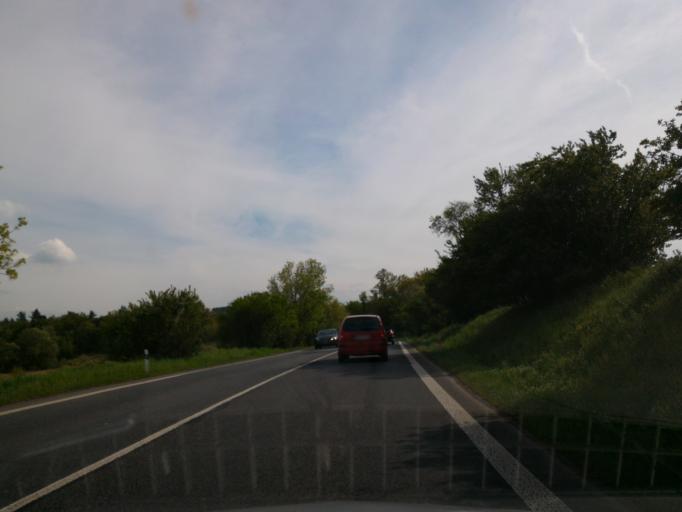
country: CZ
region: Liberecky
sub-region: Okres Ceska Lipa
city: Ceska Lipa
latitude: 50.6250
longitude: 14.5357
